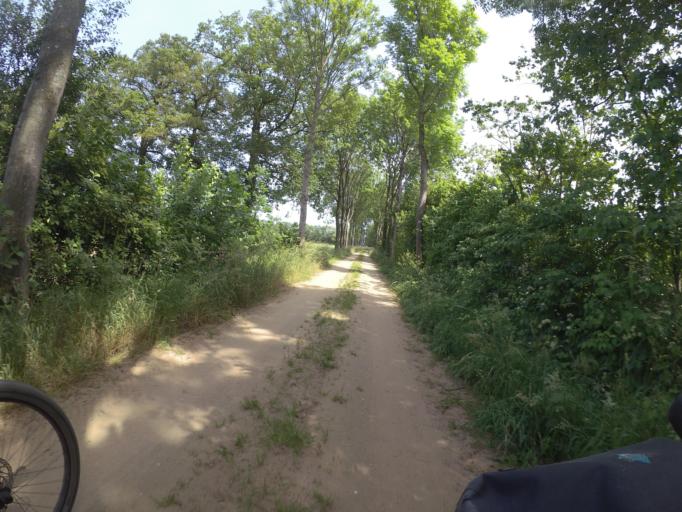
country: NL
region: Gelderland
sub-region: Gemeente Aalten
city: Aalten
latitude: 51.9417
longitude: 6.5269
